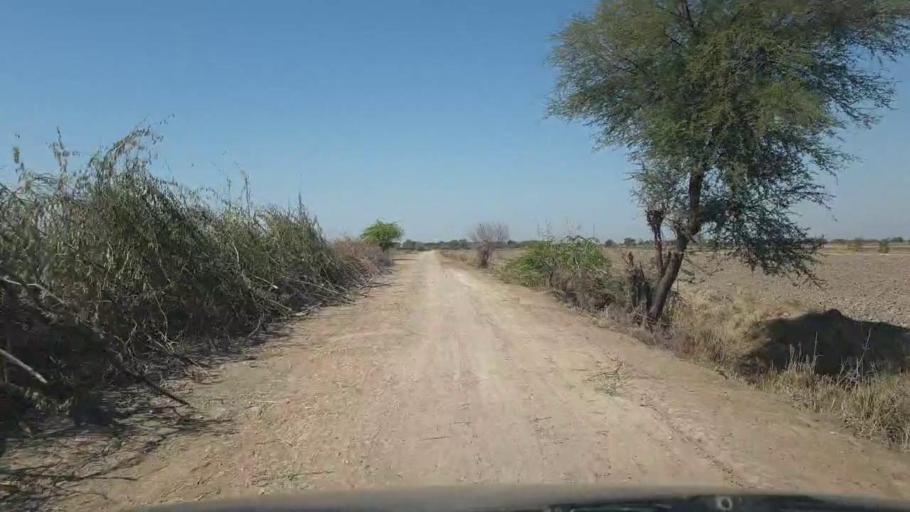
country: PK
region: Sindh
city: Dhoro Naro
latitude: 25.4496
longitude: 69.6133
